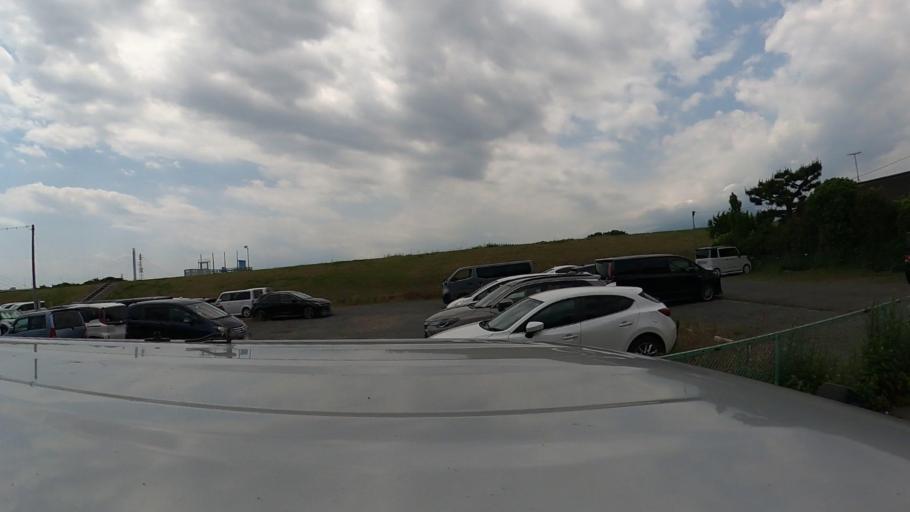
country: JP
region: Kanagawa
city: Chigasaki
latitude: 35.3569
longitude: 139.3729
